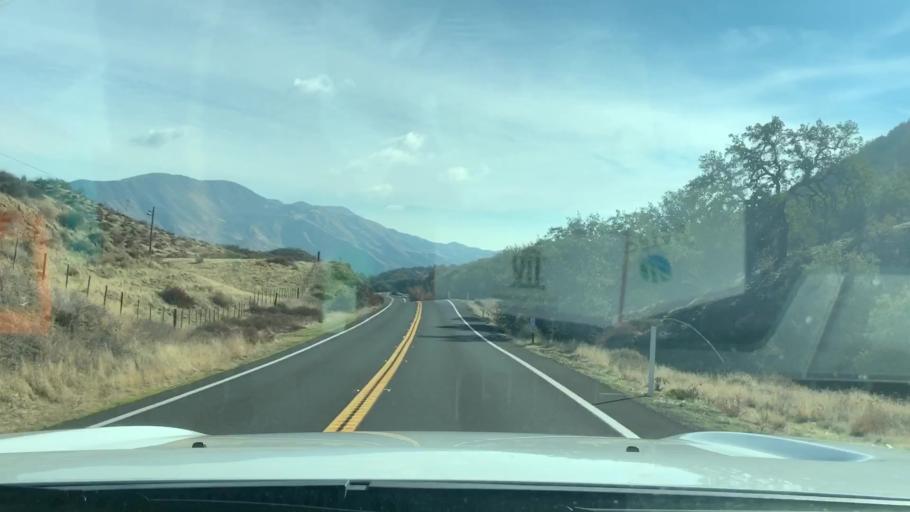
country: US
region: California
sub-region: Fresno County
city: Coalinga
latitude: 36.0898
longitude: -120.5008
